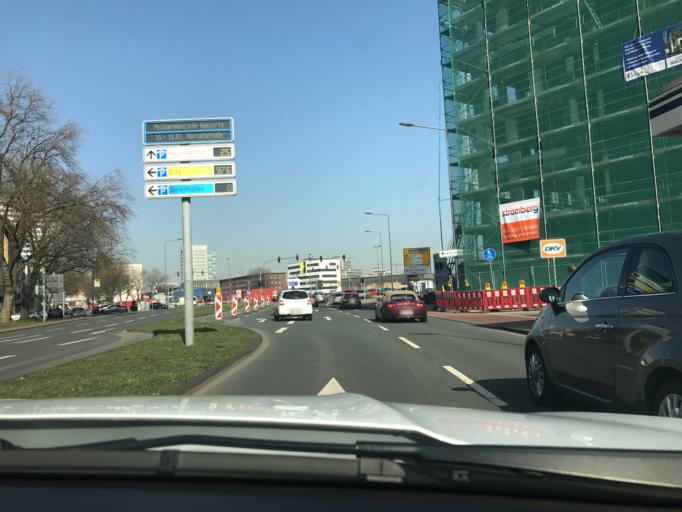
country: DE
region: North Rhine-Westphalia
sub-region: Regierungsbezirk Dusseldorf
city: Duisburg
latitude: 51.4267
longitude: 6.7693
